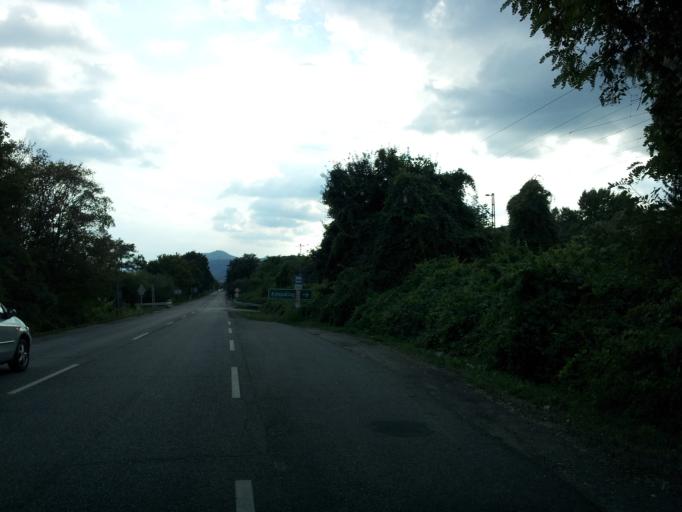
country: HU
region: Pest
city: Kismaros
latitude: 47.8217
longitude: 18.9862
